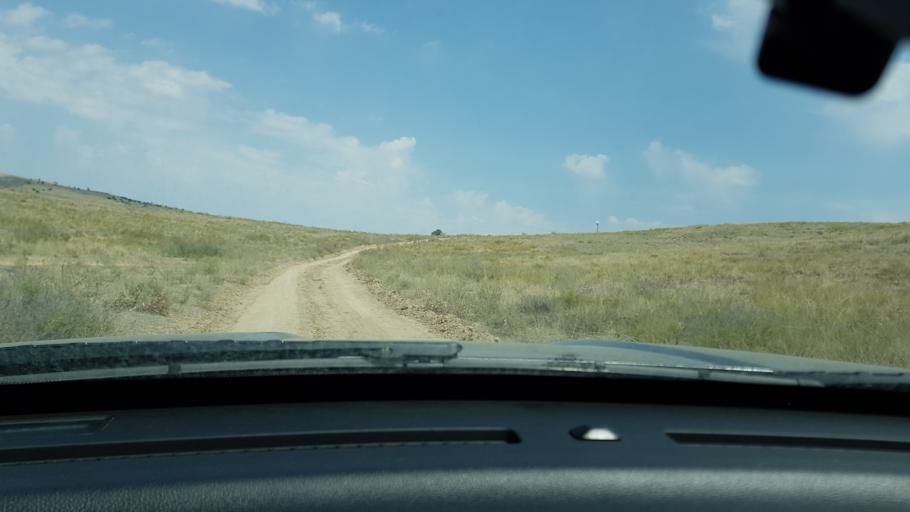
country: TM
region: Ahal
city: Baharly
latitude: 38.4088
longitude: 56.9127
